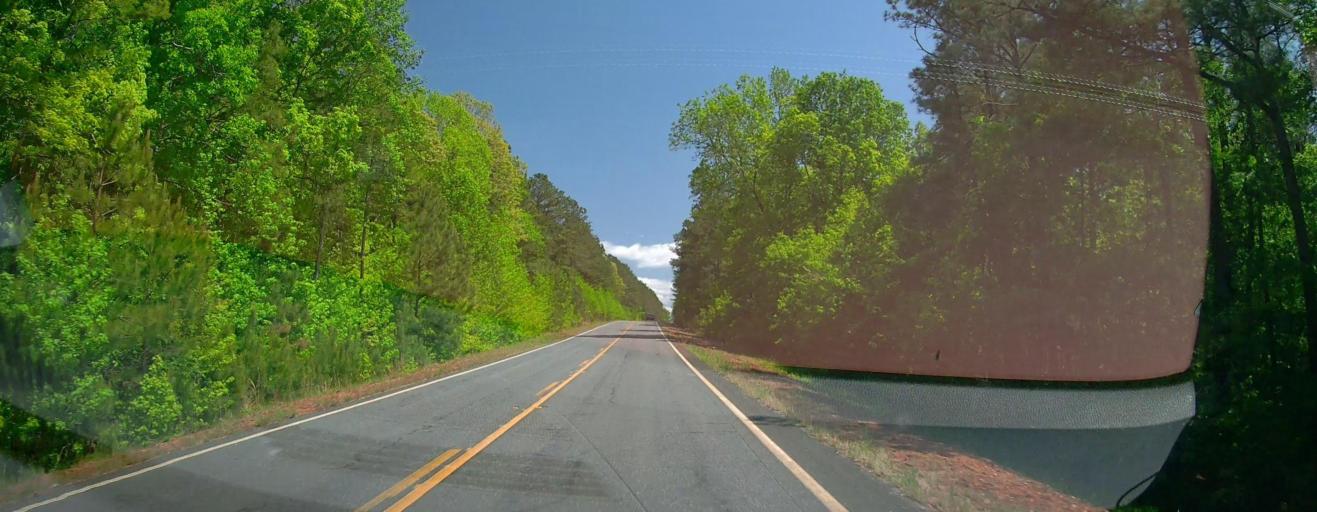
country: US
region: Georgia
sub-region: Putnam County
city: Eatonton
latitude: 33.2186
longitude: -83.4897
